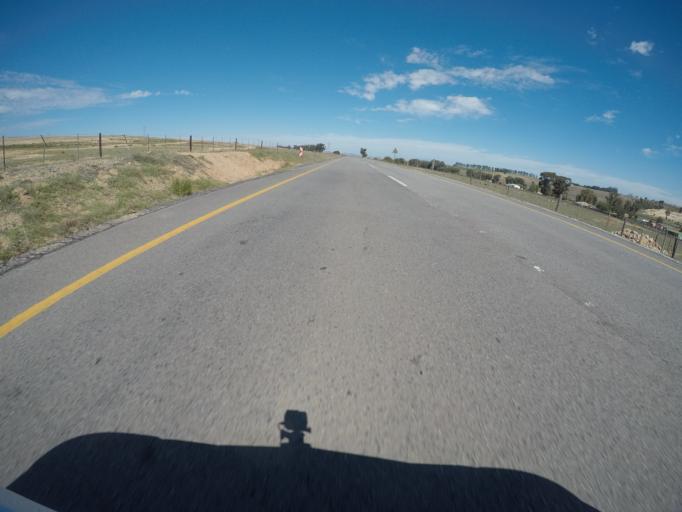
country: ZA
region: Western Cape
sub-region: West Coast District Municipality
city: Malmesbury
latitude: -33.4981
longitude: 18.6807
